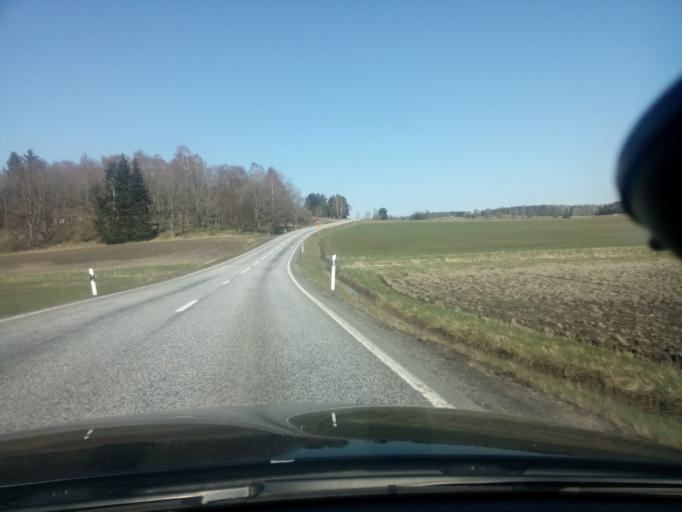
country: SE
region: Soedermanland
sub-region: Nykopings Kommun
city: Stigtomta
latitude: 58.9176
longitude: 16.8216
